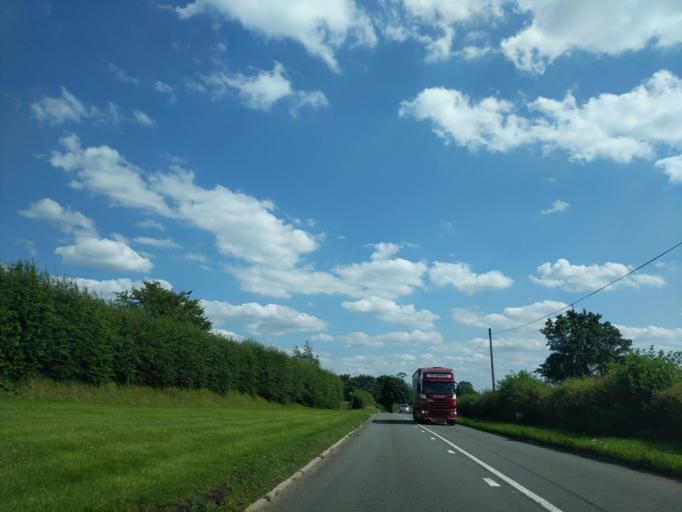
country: GB
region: England
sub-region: Staffordshire
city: Uttoxeter
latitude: 52.9288
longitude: -1.9206
